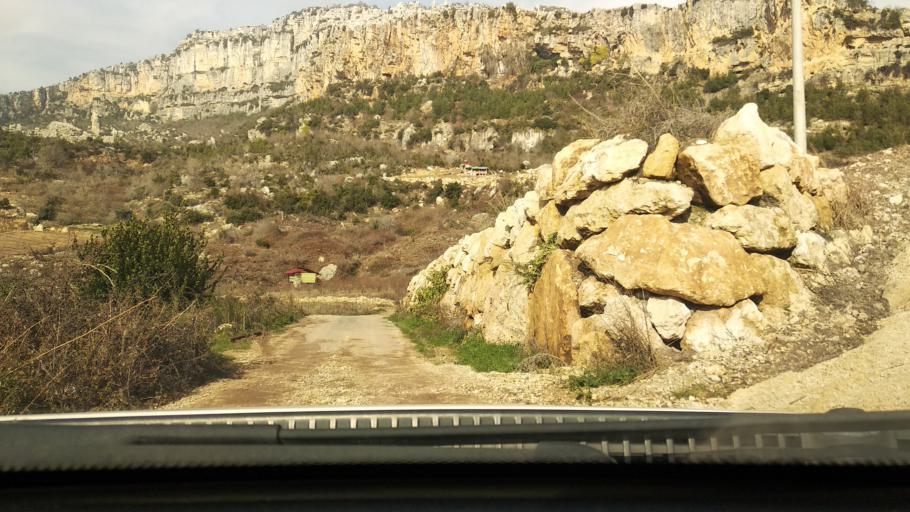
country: TR
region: Mersin
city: Kuzucubelen
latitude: 36.8764
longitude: 34.4729
